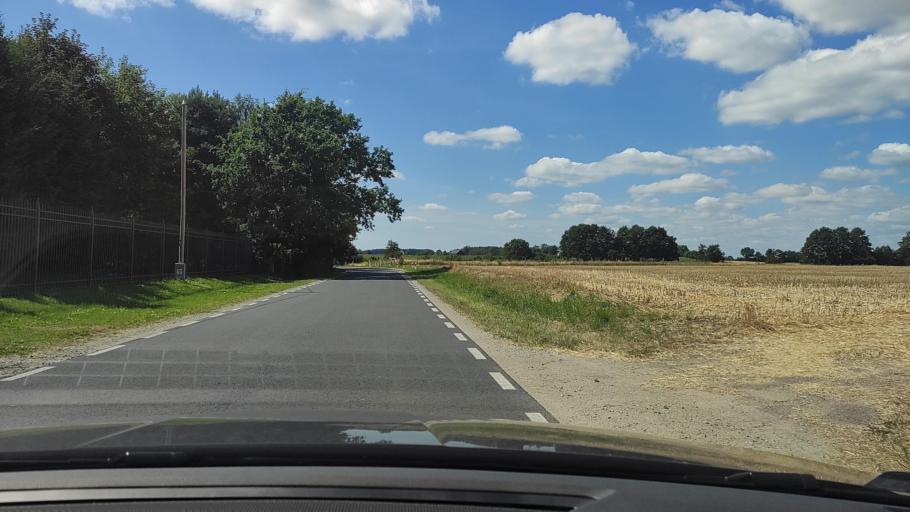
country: PL
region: Greater Poland Voivodeship
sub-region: Powiat poznanski
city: Kostrzyn
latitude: 52.4810
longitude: 17.1727
